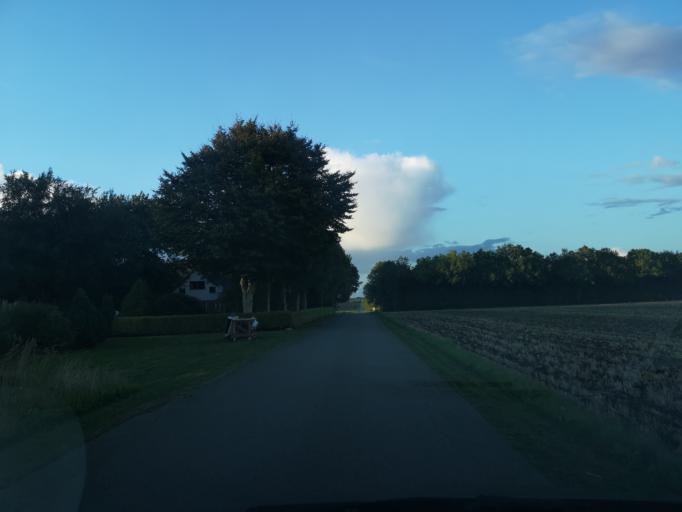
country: DK
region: Central Jutland
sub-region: Ringkobing-Skjern Kommune
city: Videbaek
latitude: 56.0309
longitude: 8.5735
